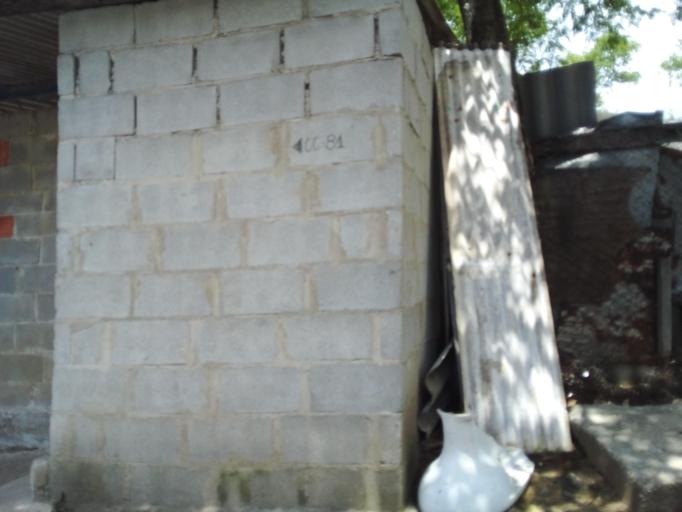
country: BR
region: Espirito Santo
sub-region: Serra
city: Serra
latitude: -20.2177
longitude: -40.2789
